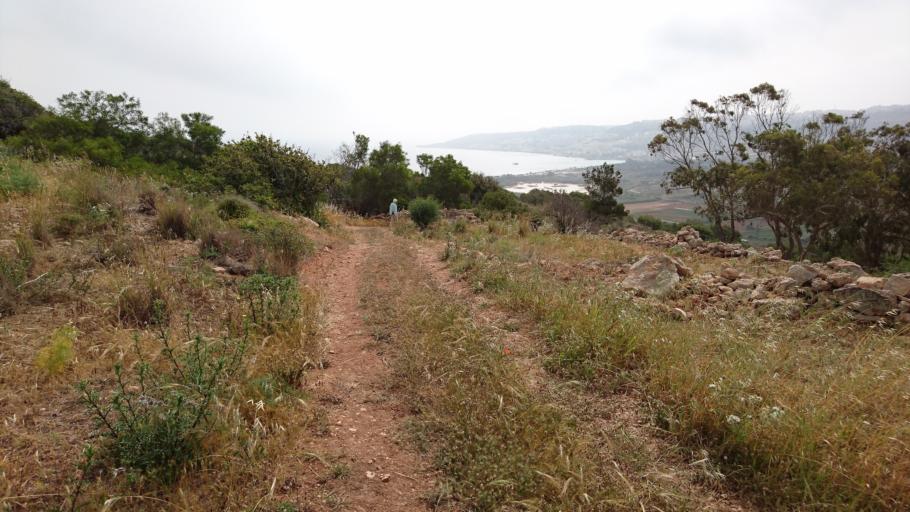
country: MT
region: Il-Mellieha
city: Mellieha
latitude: 35.9718
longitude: 14.3379
